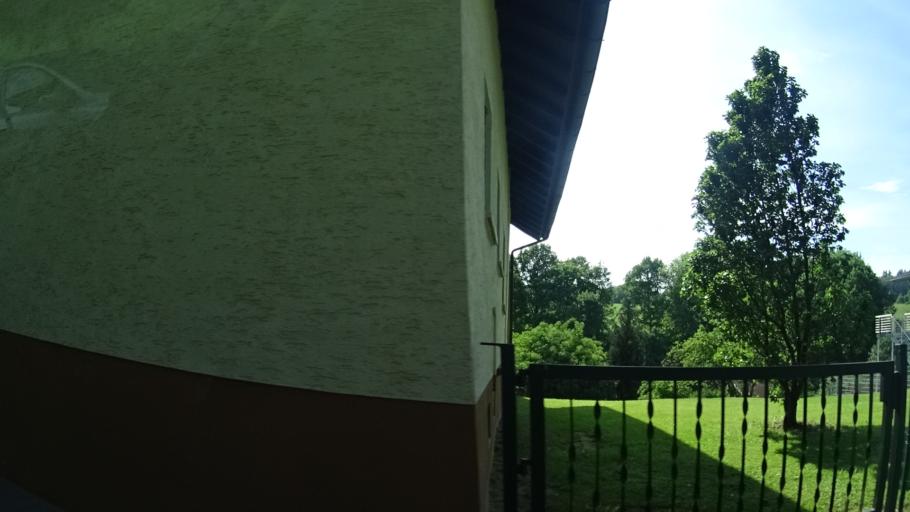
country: DE
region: Hesse
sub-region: Regierungsbezirk Darmstadt
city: Wald-Michelbach
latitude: 49.6213
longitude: 8.8333
